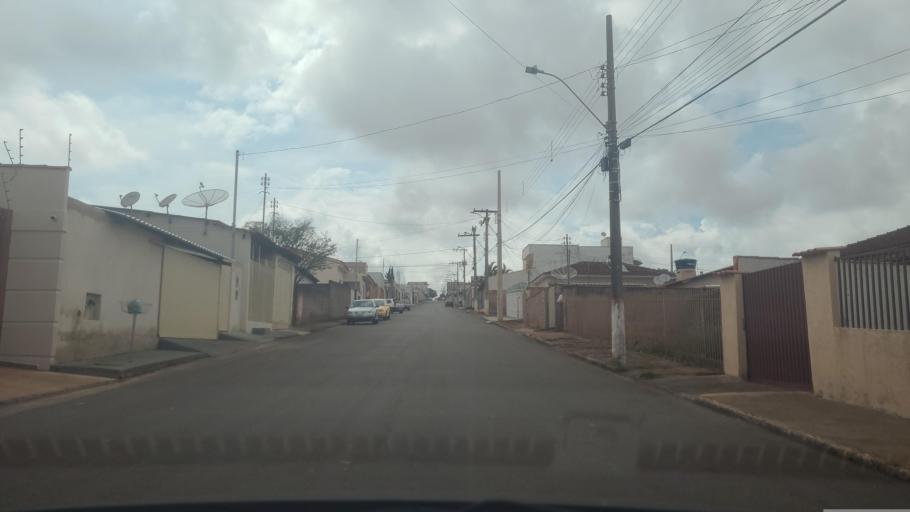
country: BR
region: Minas Gerais
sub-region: Carmo Do Paranaiba
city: Carmo do Paranaiba
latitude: -19.1960
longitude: -46.2438
